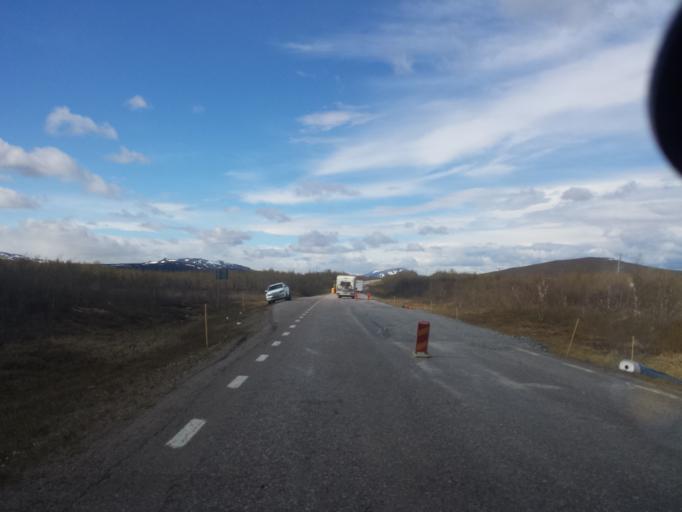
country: SE
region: Norrbotten
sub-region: Kiruna Kommun
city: Kiruna
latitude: 68.0131
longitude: 19.8419
